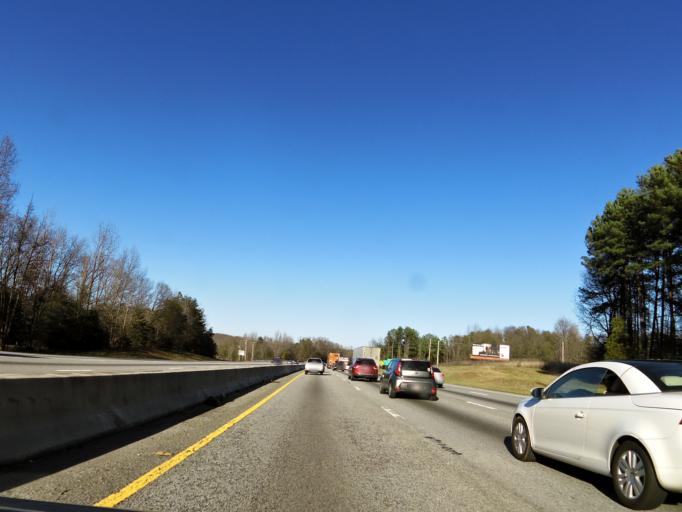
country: US
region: South Carolina
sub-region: Greenville County
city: Five Forks
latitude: 34.8476
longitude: -82.2799
